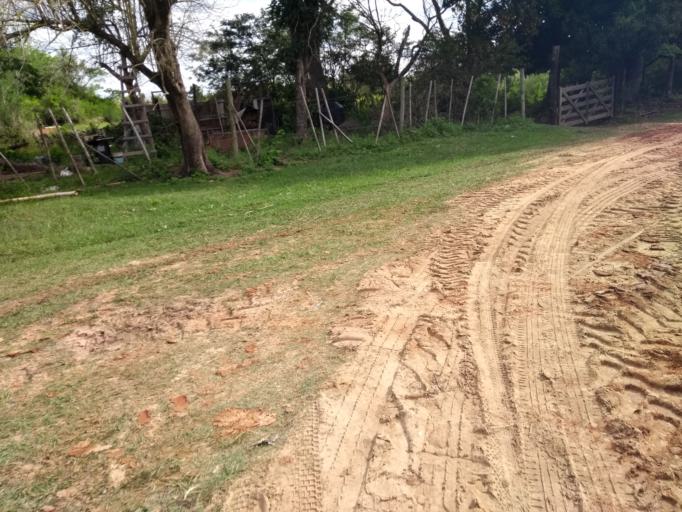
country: AR
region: Corrientes
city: San Luis del Palmar
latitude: -27.4588
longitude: -58.6574
